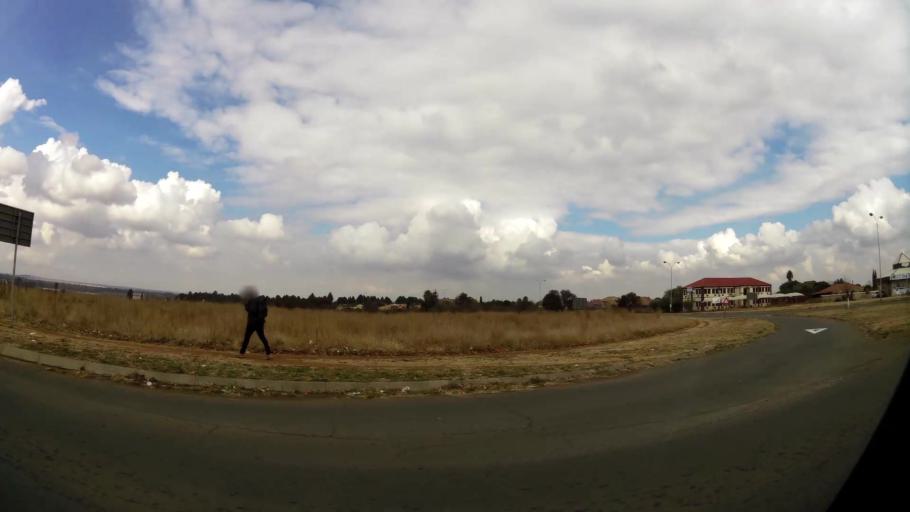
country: ZA
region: Gauteng
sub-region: Sedibeng District Municipality
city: Vanderbijlpark
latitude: -26.7294
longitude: 27.8636
